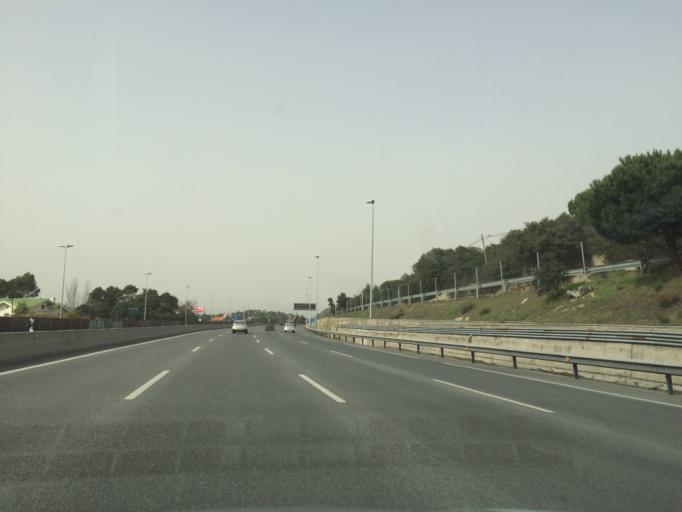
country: ES
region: Madrid
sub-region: Provincia de Madrid
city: Torrelodones
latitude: 40.5842
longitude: -3.9510
